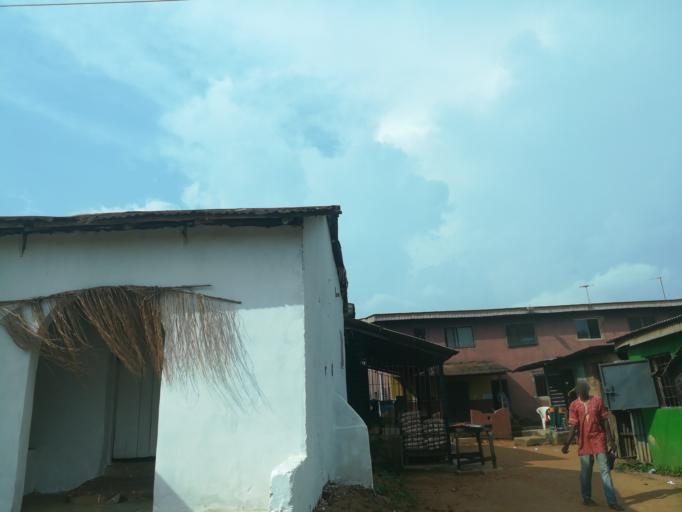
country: NG
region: Lagos
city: Ikorodu
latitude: 6.6646
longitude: 3.6724
